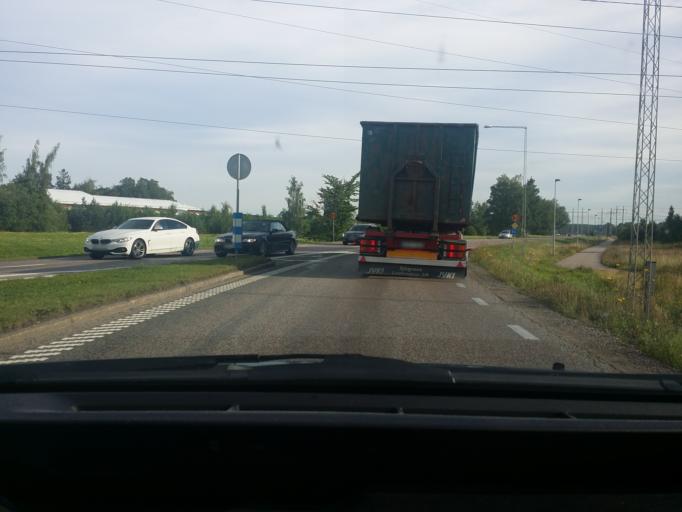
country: SE
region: Vaestmanland
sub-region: Vasteras
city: Hokasen
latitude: 59.6454
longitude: 16.5723
